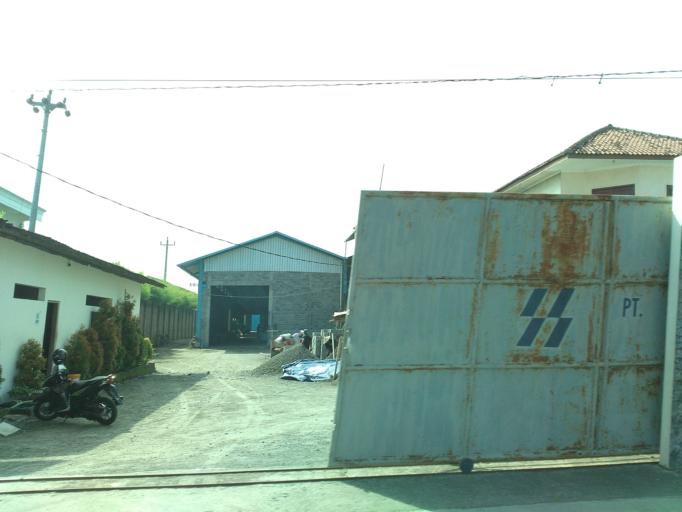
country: ID
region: Central Java
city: Ceper
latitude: -7.6635
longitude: 110.6684
